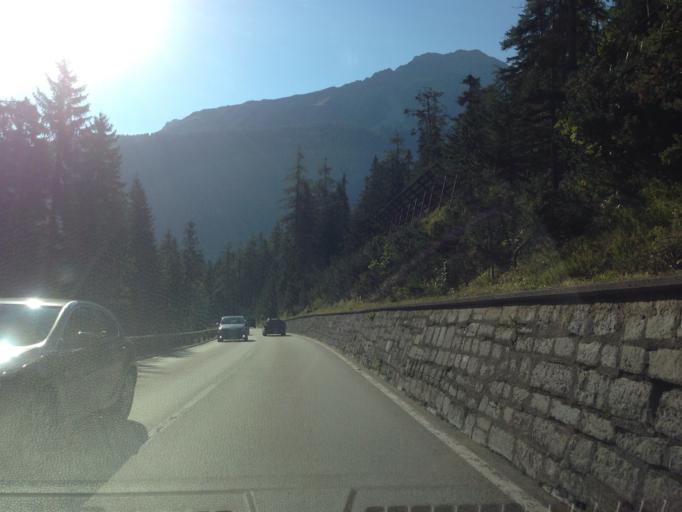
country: AT
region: Tyrol
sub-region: Politischer Bezirk Imst
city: Nassereith
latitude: 47.3627
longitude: 10.8404
